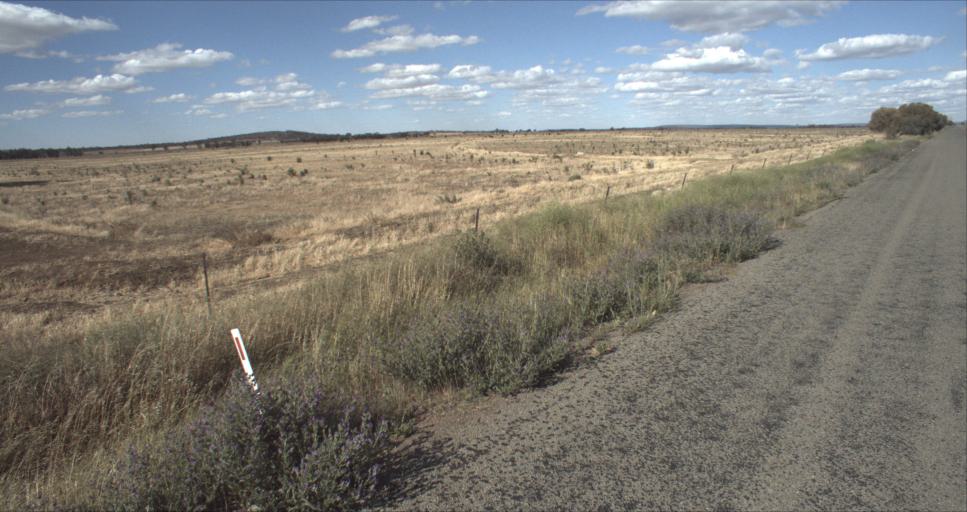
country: AU
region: New South Wales
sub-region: Leeton
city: Leeton
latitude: -34.4406
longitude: 146.2265
